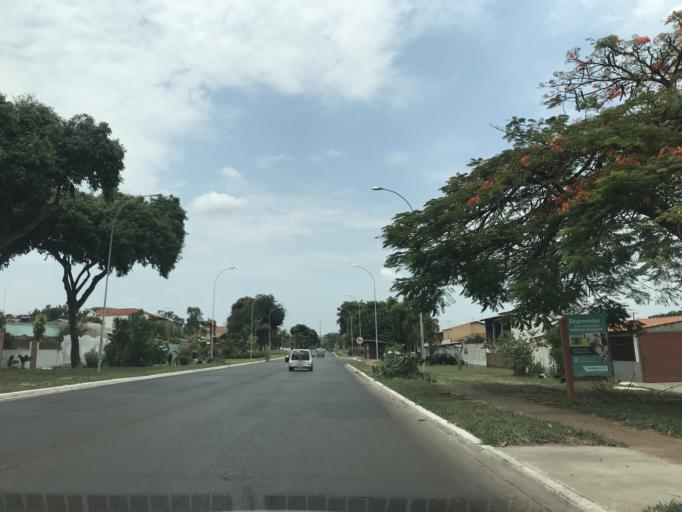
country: BR
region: Federal District
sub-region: Brasilia
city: Brasilia
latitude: -15.6494
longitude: -47.8036
